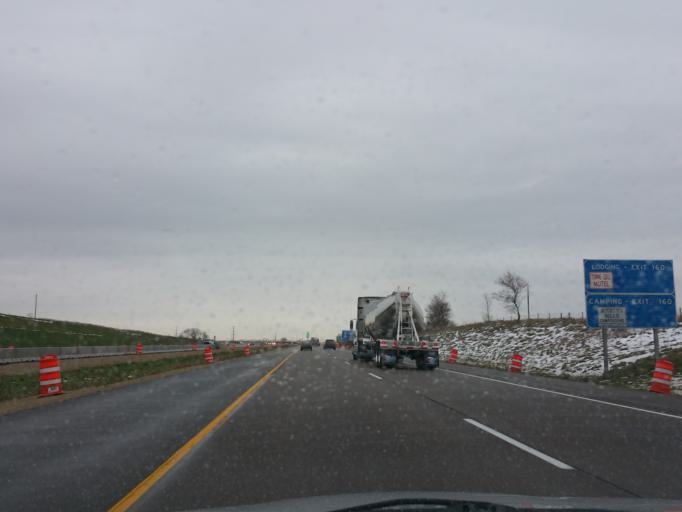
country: US
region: Wisconsin
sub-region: Rock County
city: Edgerton
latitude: 42.8815
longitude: -89.0642
